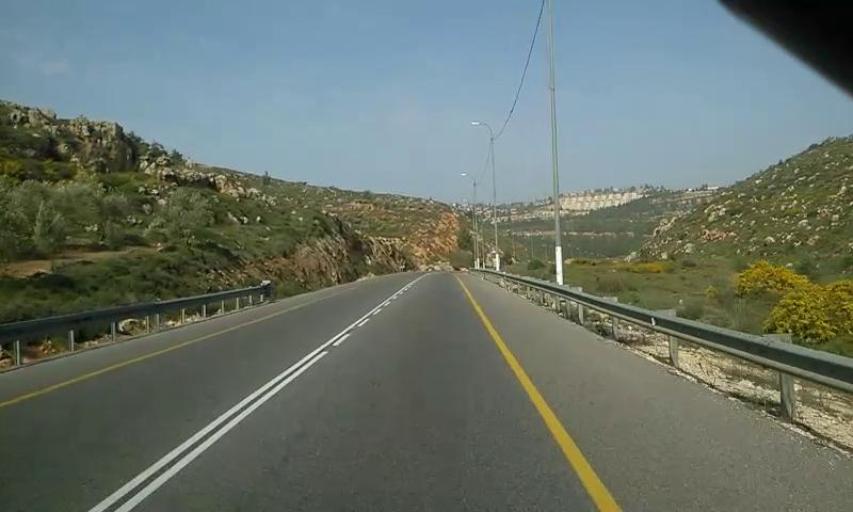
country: PS
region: West Bank
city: Qaryut
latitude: 32.0642
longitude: 35.2756
